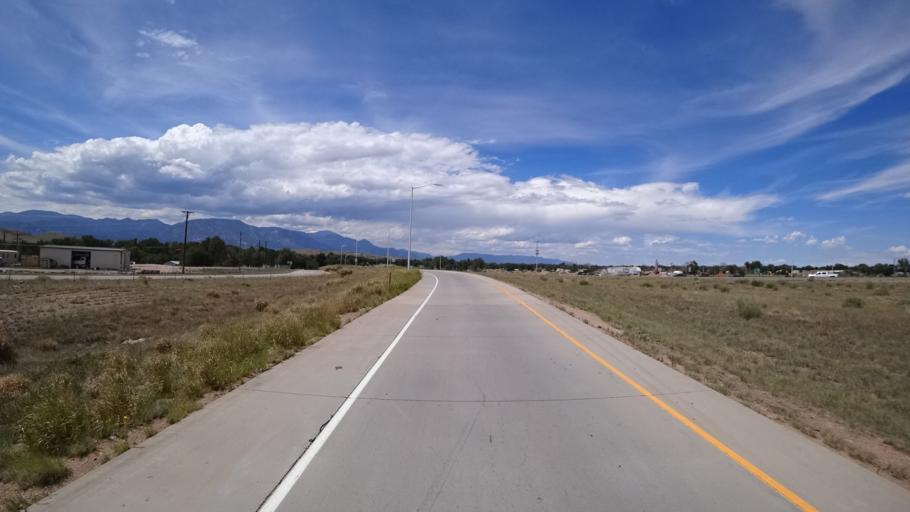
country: US
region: Colorado
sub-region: El Paso County
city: Security-Widefield
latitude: 38.7223
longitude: -104.7209
